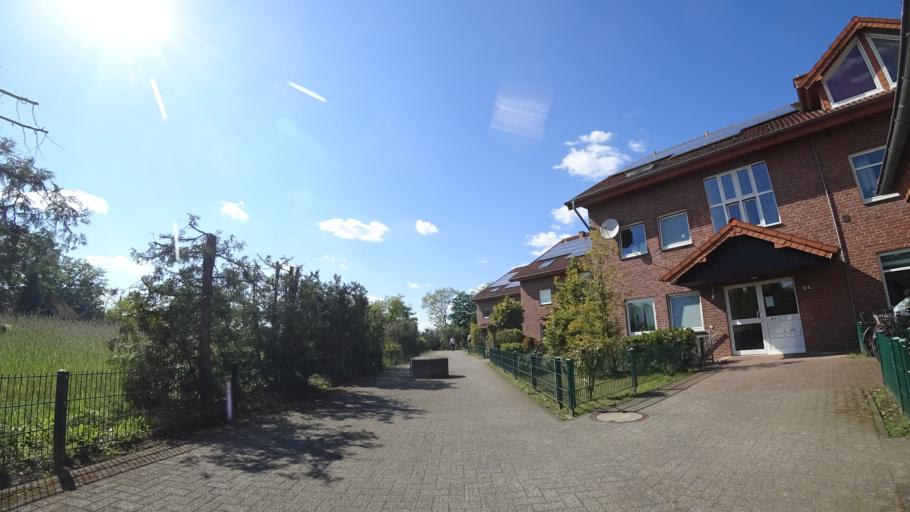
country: DE
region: North Rhine-Westphalia
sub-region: Regierungsbezirk Detmold
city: Guetersloh
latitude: 51.8863
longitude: 8.3512
